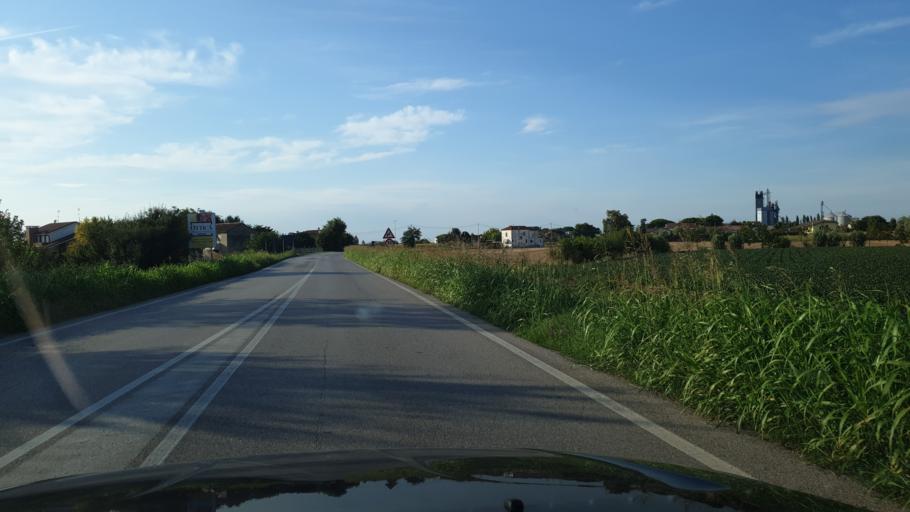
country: IT
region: Veneto
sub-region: Provincia di Rovigo
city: Fiesso Umbertiano
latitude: 44.9666
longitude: 11.6116
